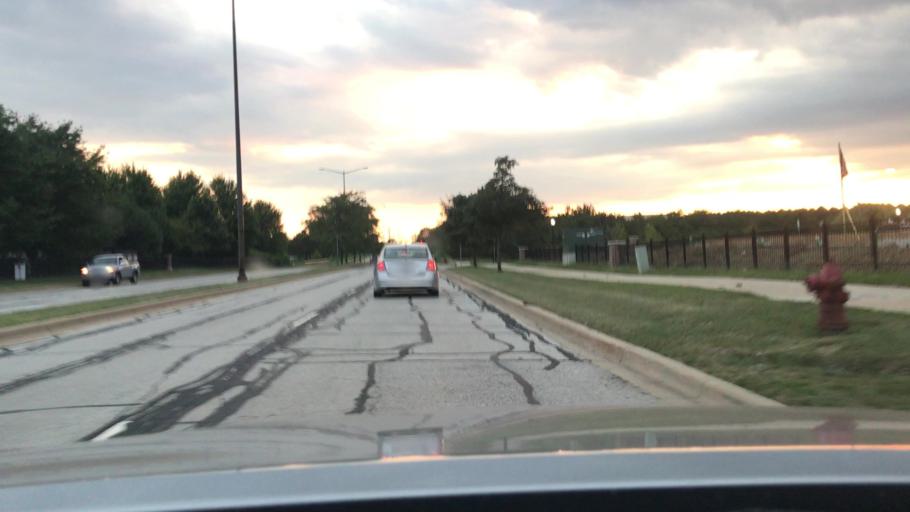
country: US
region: Illinois
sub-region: DuPage County
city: Warrenville
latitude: 41.7694
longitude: -88.2146
